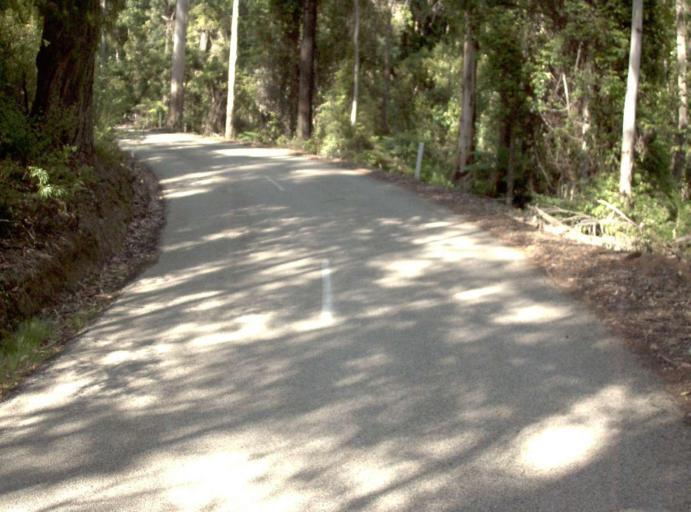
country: AU
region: Victoria
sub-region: East Gippsland
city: Lakes Entrance
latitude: -37.4338
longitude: 148.5963
